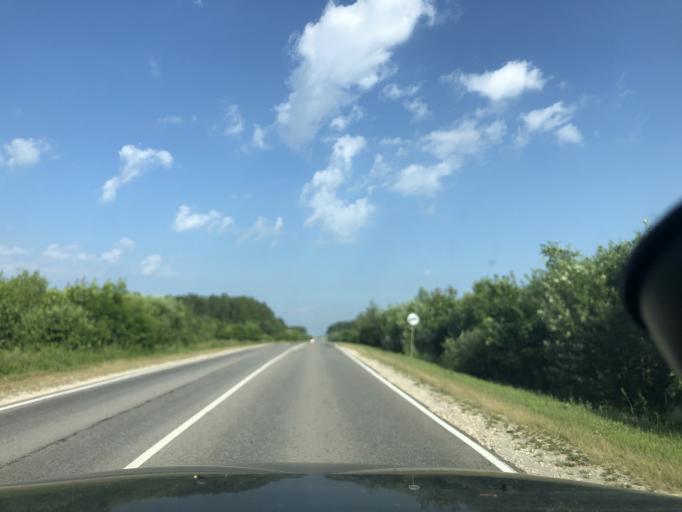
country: RU
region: Tula
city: Dubna
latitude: 54.1345
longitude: 37.0246
